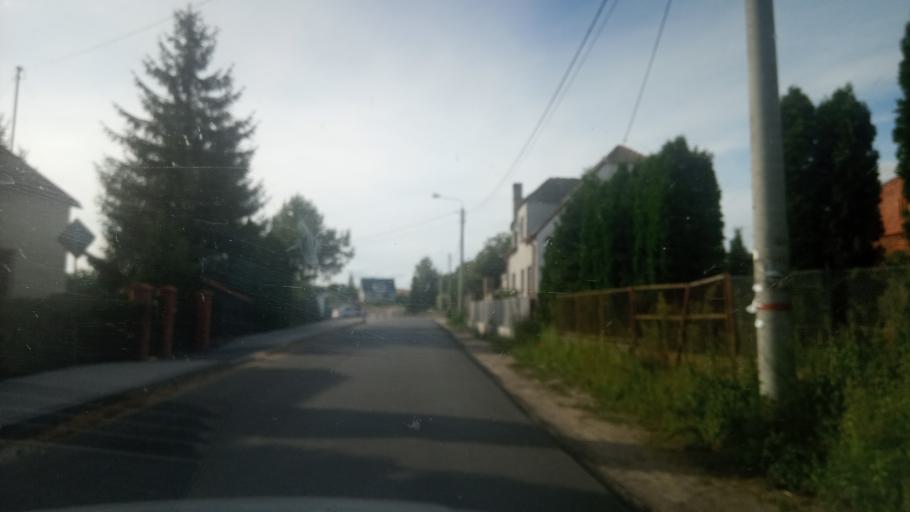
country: PL
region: Kujawsko-Pomorskie
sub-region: Powiat nakielski
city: Sadki
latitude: 53.1952
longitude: 17.3888
